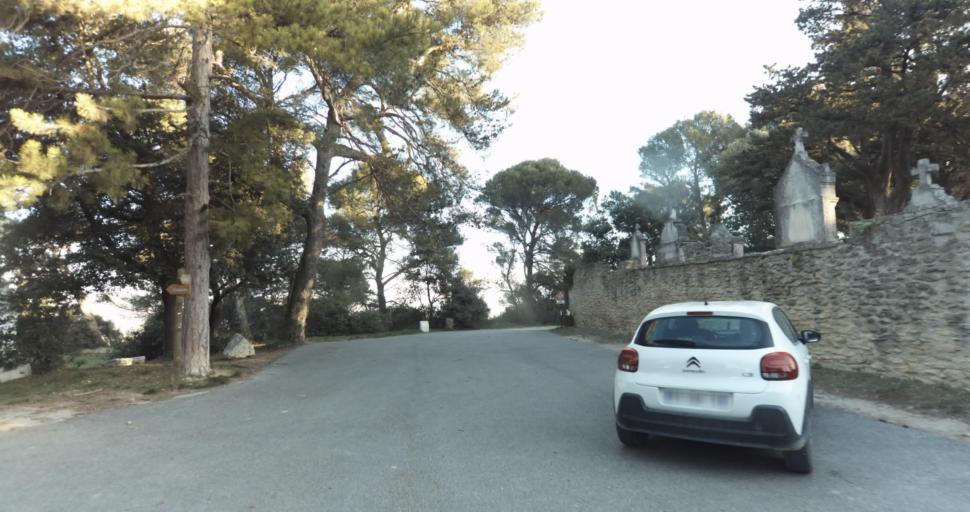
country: FR
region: Provence-Alpes-Cote d'Azur
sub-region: Departement des Bouches-du-Rhone
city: Barbentane
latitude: 43.8977
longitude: 4.7503
